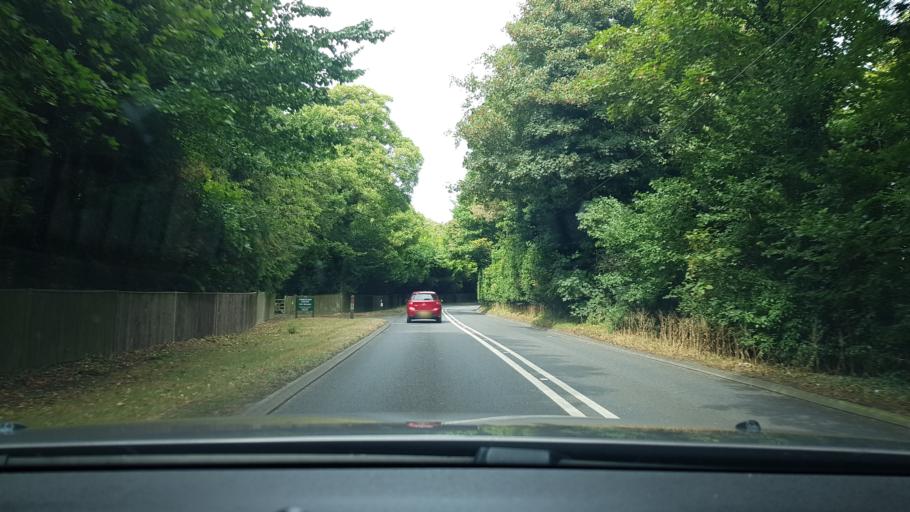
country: GB
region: England
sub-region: West Berkshire
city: Hungerford
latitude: 51.4323
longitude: -1.4997
